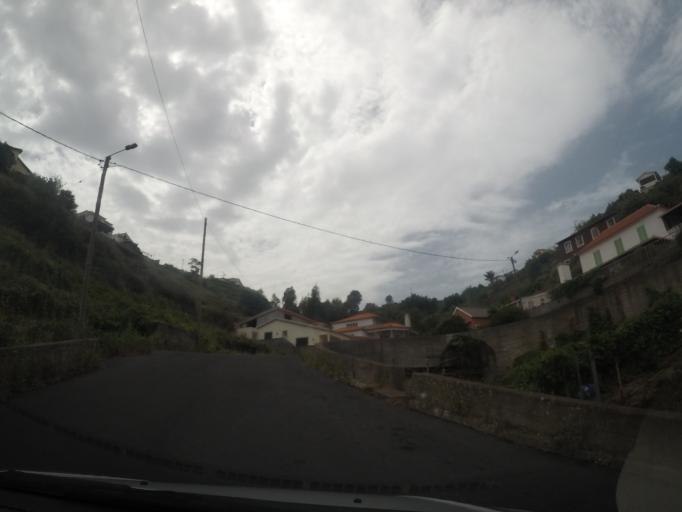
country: PT
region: Madeira
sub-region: Santa Cruz
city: Santa Cruz
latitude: 32.6870
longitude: -16.8089
